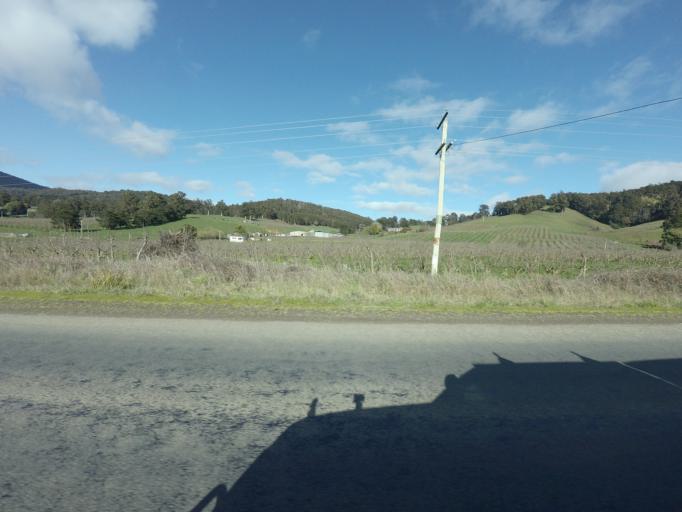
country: AU
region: Tasmania
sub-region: Huon Valley
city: Geeveston
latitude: -43.1884
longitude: 146.9583
